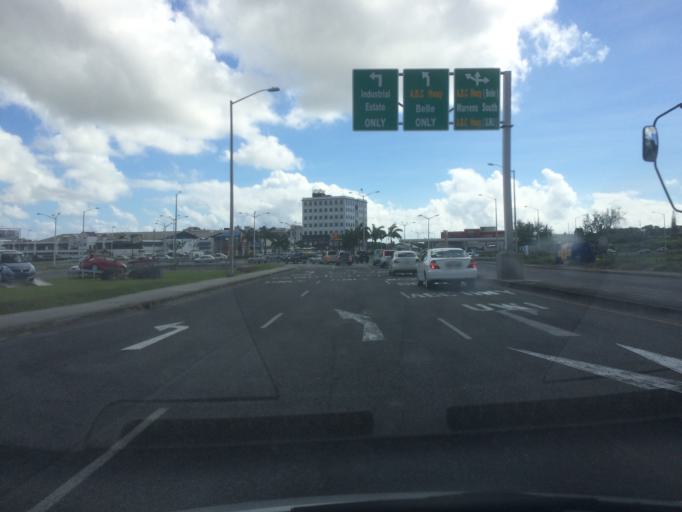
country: BB
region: Saint Michael
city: Bridgetown
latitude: 13.1443
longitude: -59.6100
